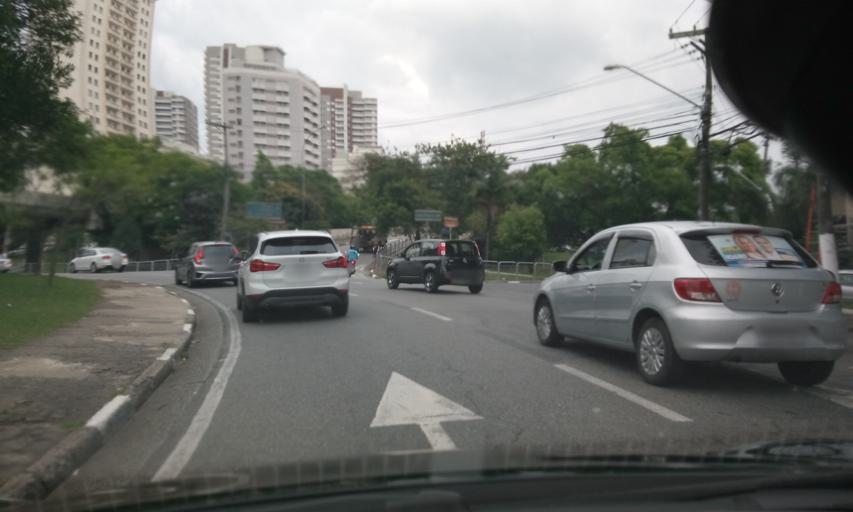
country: BR
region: Sao Paulo
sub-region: Sao Bernardo Do Campo
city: Sao Bernardo do Campo
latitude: -23.6893
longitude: -46.5605
